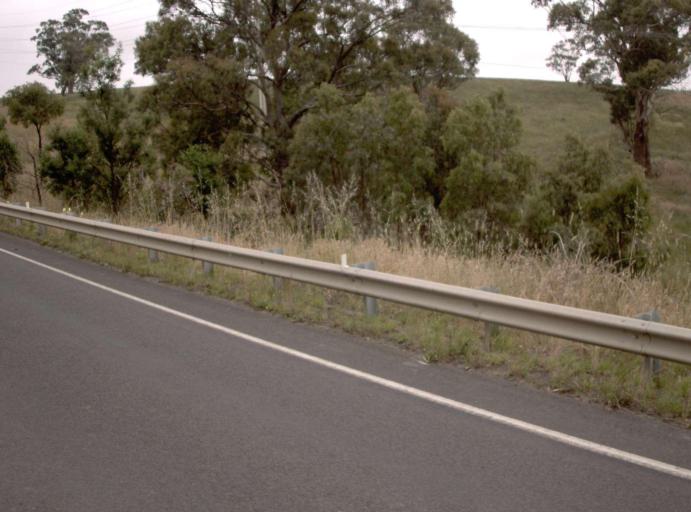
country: AU
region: Victoria
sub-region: Latrobe
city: Traralgon
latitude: -38.2480
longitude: 146.5262
